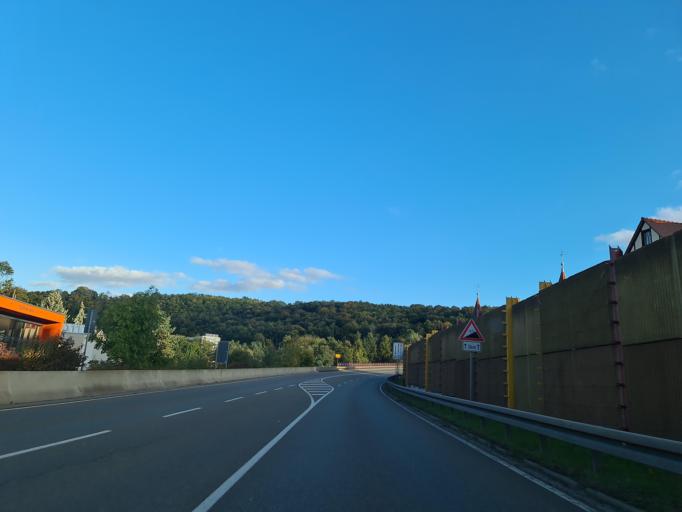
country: DE
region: Thuringia
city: Weida
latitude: 50.7793
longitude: 12.0652
